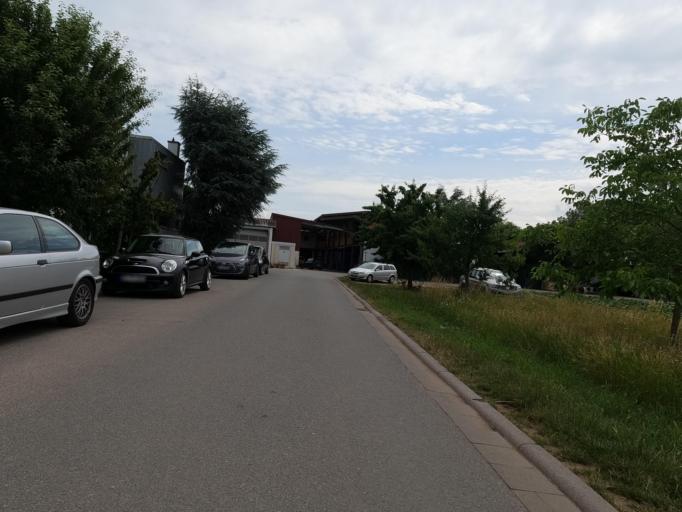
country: DE
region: Hesse
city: Weiterstadt
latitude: 49.9330
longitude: 8.6041
